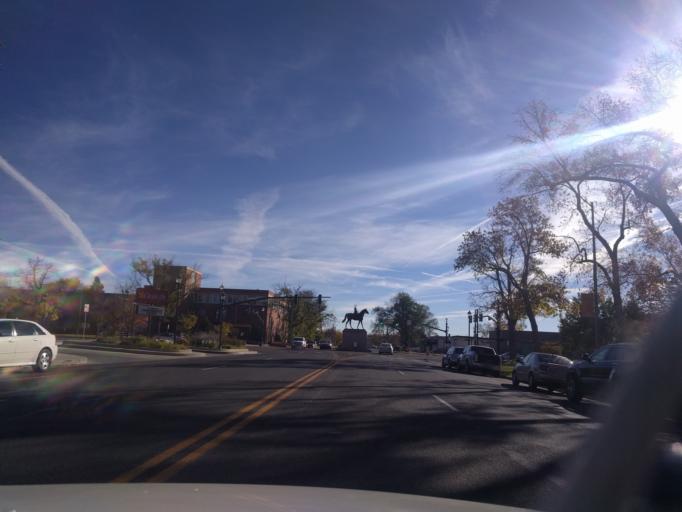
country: US
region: Colorado
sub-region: El Paso County
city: Colorado Springs
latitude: 38.8381
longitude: -104.8224
